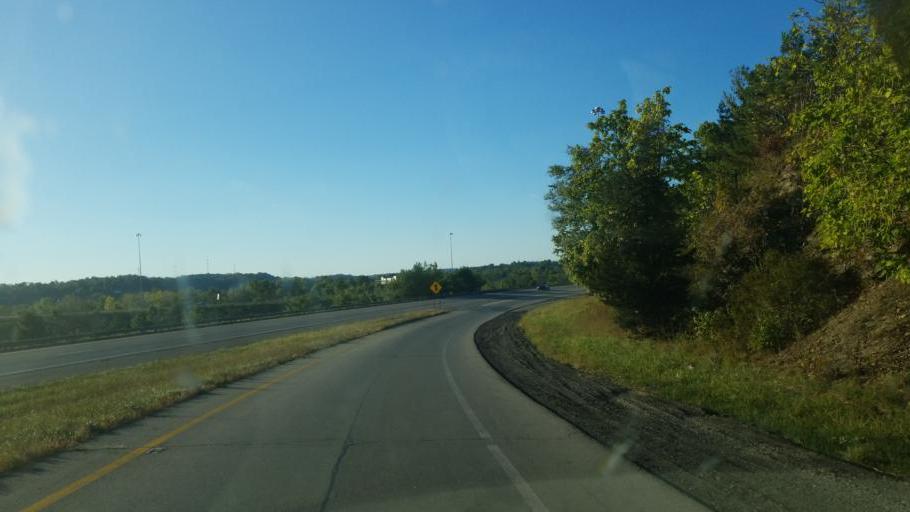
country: US
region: Ohio
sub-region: Guernsey County
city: Byesville
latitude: 40.0010
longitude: -81.5585
